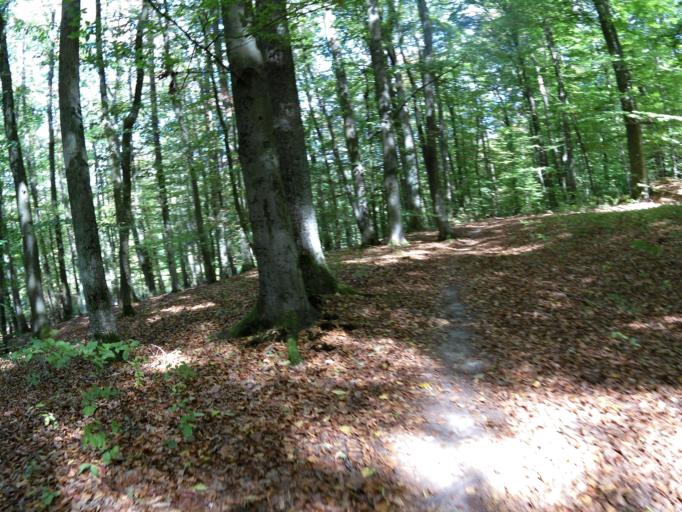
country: DE
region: Bavaria
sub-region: Regierungsbezirk Unterfranken
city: Waldbuttelbrunn
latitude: 49.7701
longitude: 9.8480
